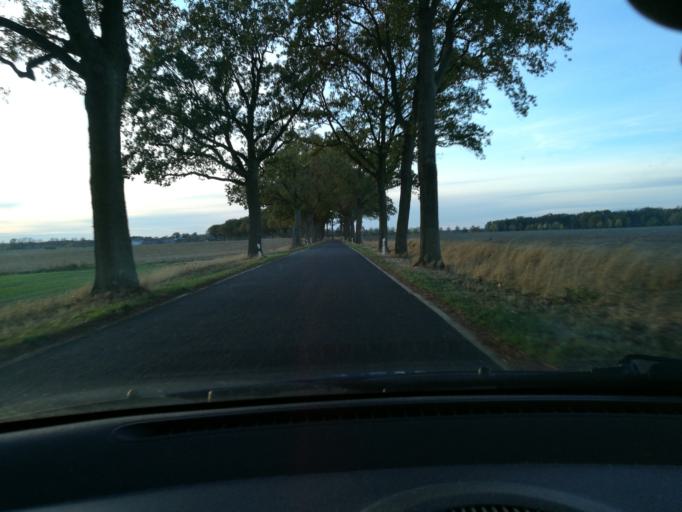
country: DE
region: Brandenburg
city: Karstadt
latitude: 53.0965
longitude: 11.7133
